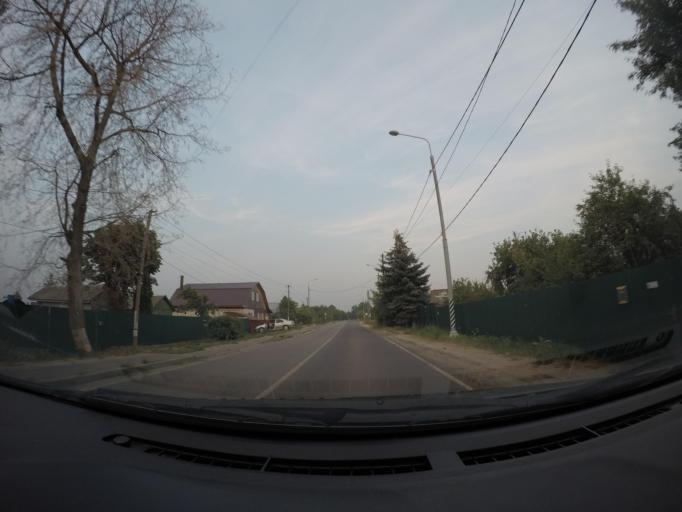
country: RU
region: Moskovskaya
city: Imeni Tsyurupy
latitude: 55.4924
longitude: 38.6689
